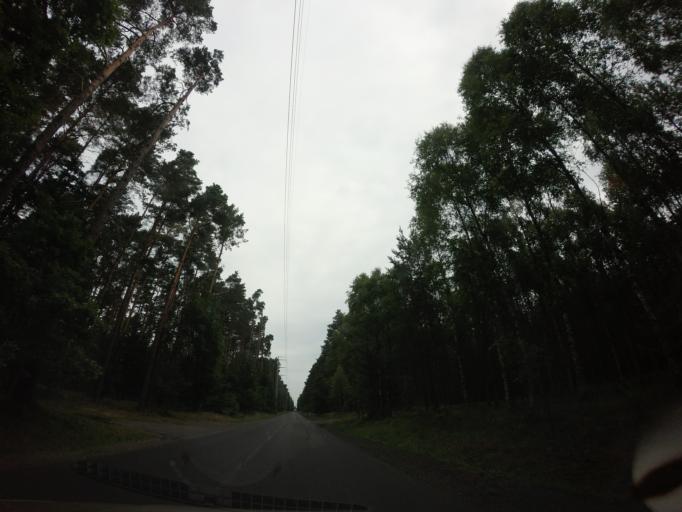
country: PL
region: West Pomeranian Voivodeship
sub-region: Powiat drawski
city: Czaplinek
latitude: 53.4738
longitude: 16.2243
